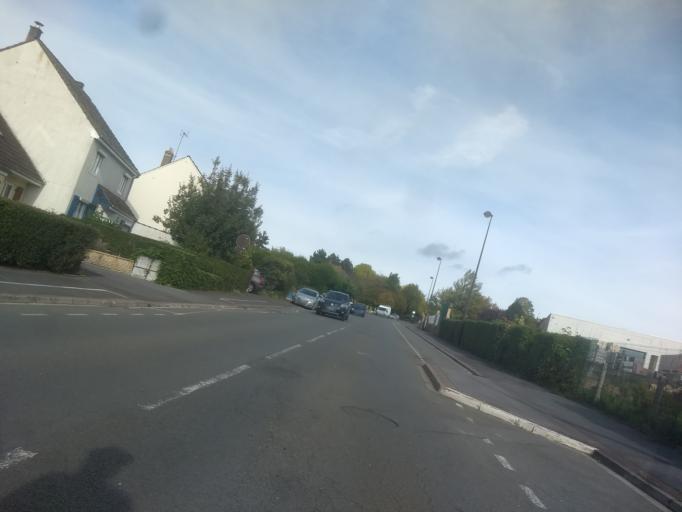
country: FR
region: Nord-Pas-de-Calais
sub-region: Departement du Pas-de-Calais
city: Dainville
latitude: 50.2910
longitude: 2.7416
